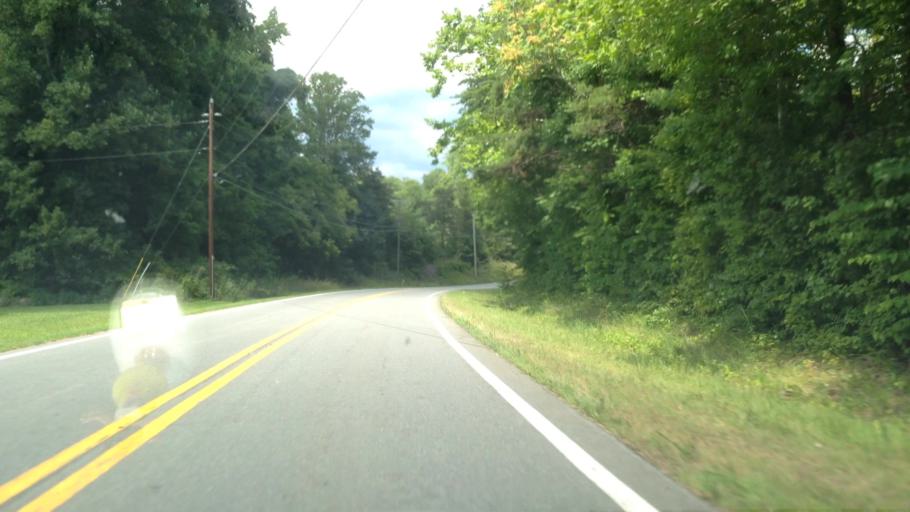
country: US
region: North Carolina
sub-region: Rockingham County
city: Reidsville
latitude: 36.4312
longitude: -79.5801
